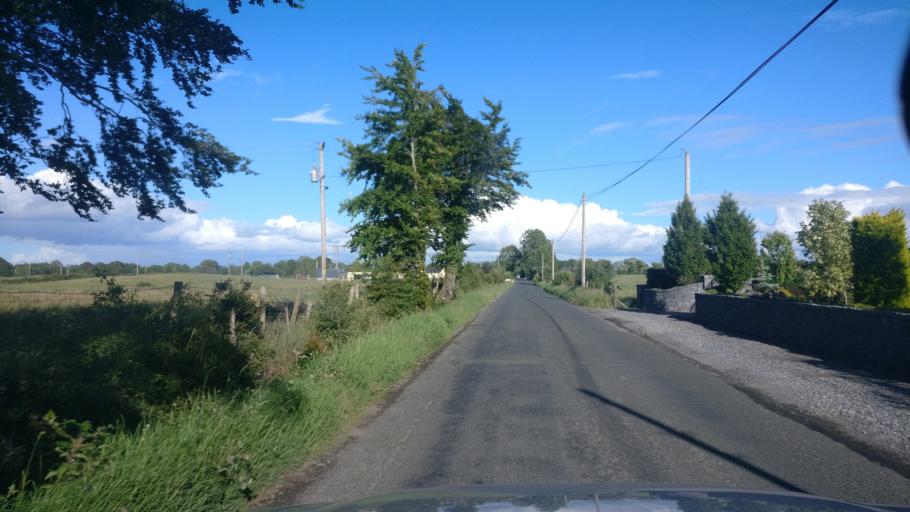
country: IE
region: Connaught
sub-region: County Galway
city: Ballinasloe
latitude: 53.2317
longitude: -8.2535
